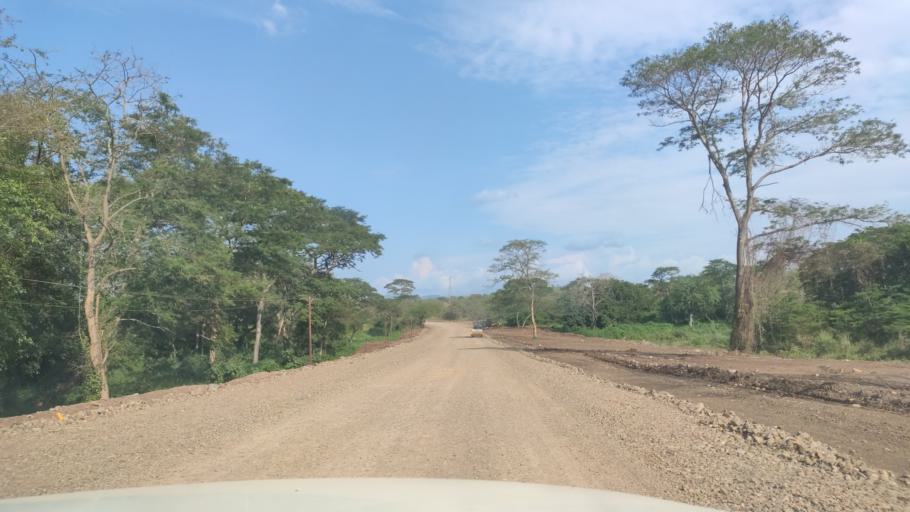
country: ET
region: Southern Nations, Nationalities, and People's Region
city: Felege Neway
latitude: 6.4284
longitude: 37.2054
